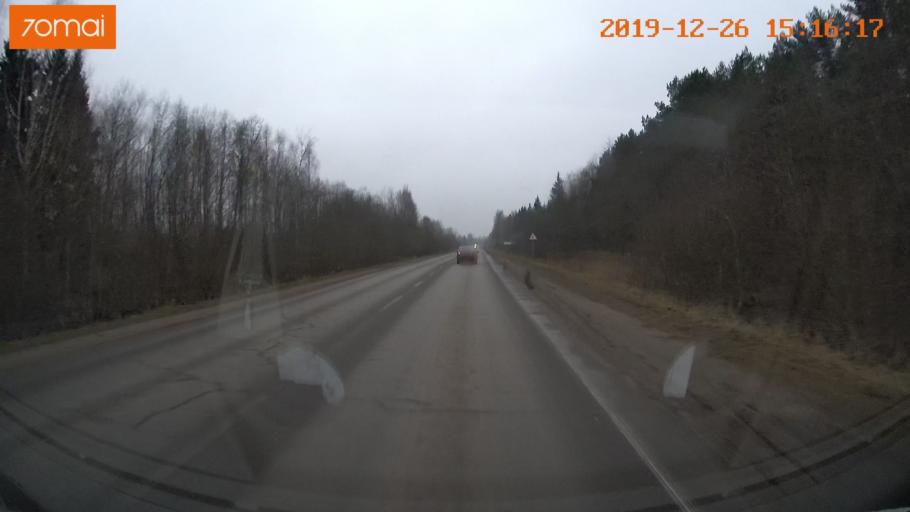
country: RU
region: Jaroslavl
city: Rybinsk
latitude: 58.0880
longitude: 38.8679
